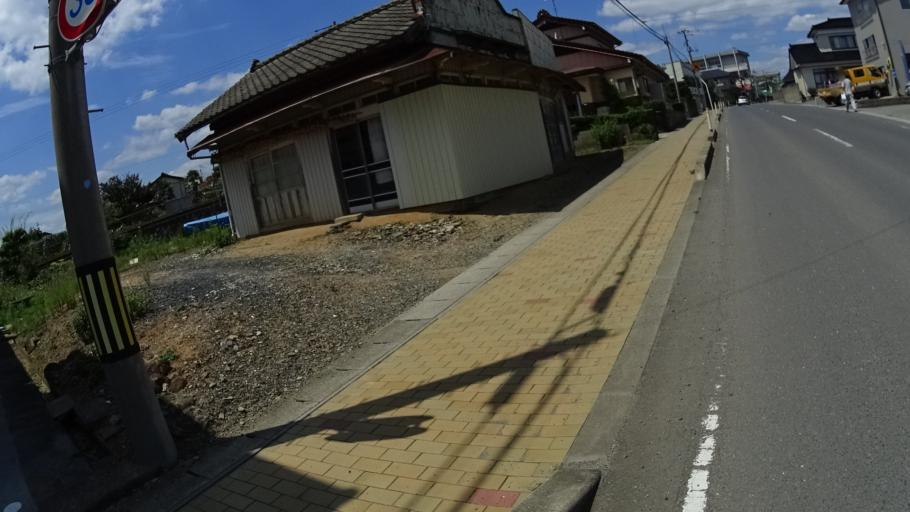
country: JP
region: Iwate
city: Ofunato
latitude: 38.8541
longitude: 141.6170
